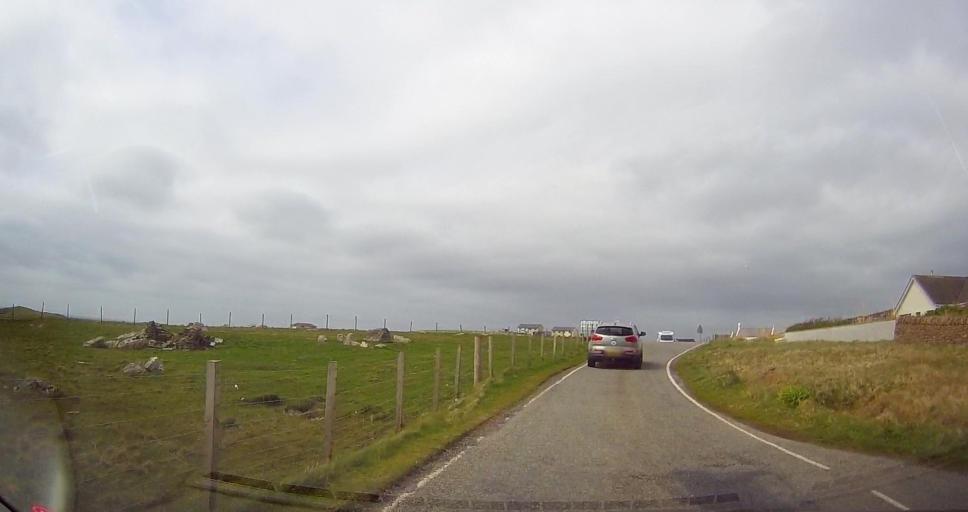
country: GB
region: Scotland
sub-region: Shetland Islands
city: Sandwick
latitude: 60.1021
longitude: -1.3237
